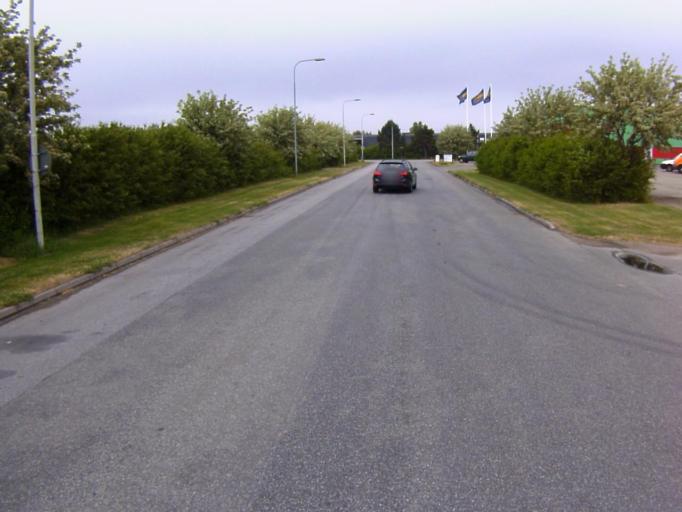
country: SE
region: Skane
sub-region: Kristianstads Kommun
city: Ahus
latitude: 55.9327
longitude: 14.2821
